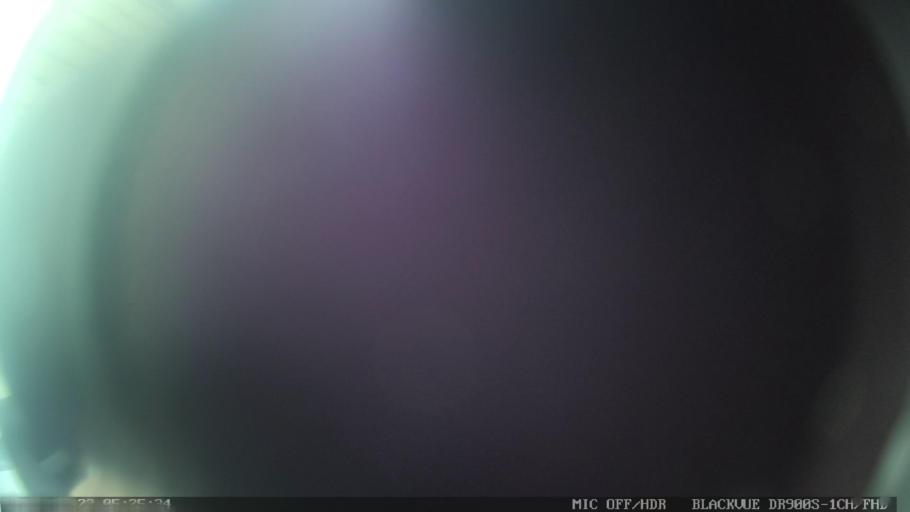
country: PT
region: Castelo Branco
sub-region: Idanha-A-Nova
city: Idanha-a-Nova
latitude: 39.9208
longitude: -7.2382
